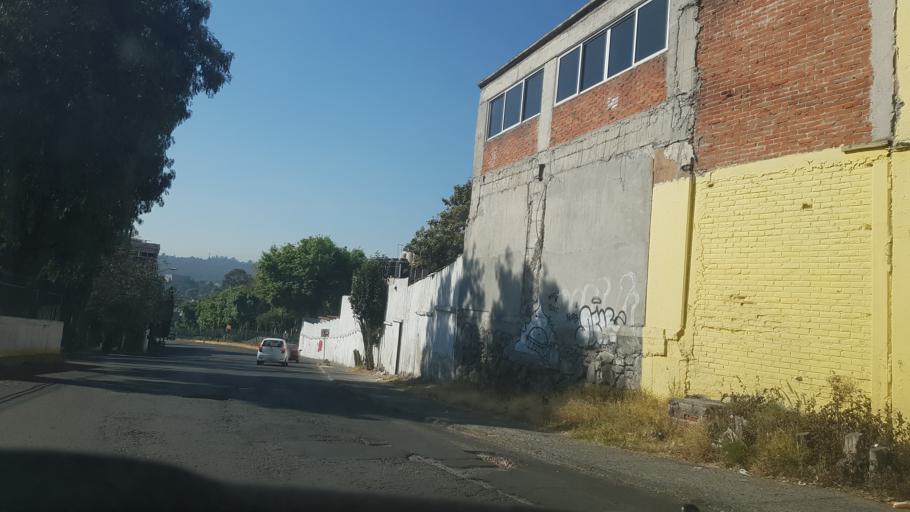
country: MX
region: Mexico
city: Naucalpan de Juarez
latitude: 19.4941
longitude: -99.2470
